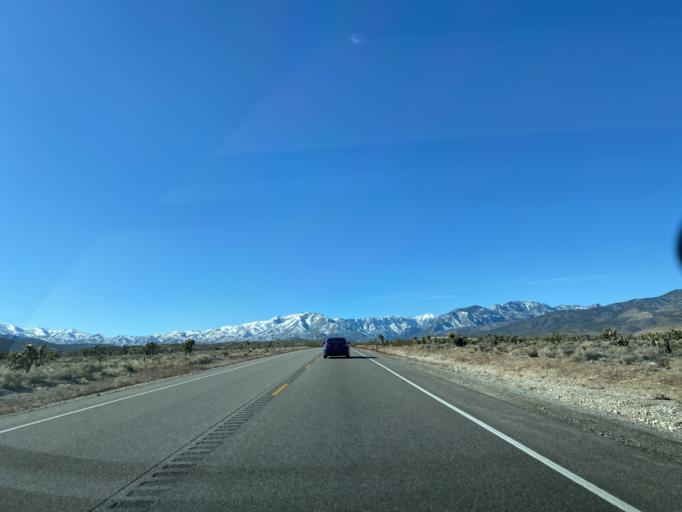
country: US
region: Nevada
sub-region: Clark County
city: Summerlin South
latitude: 36.2809
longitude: -115.4475
